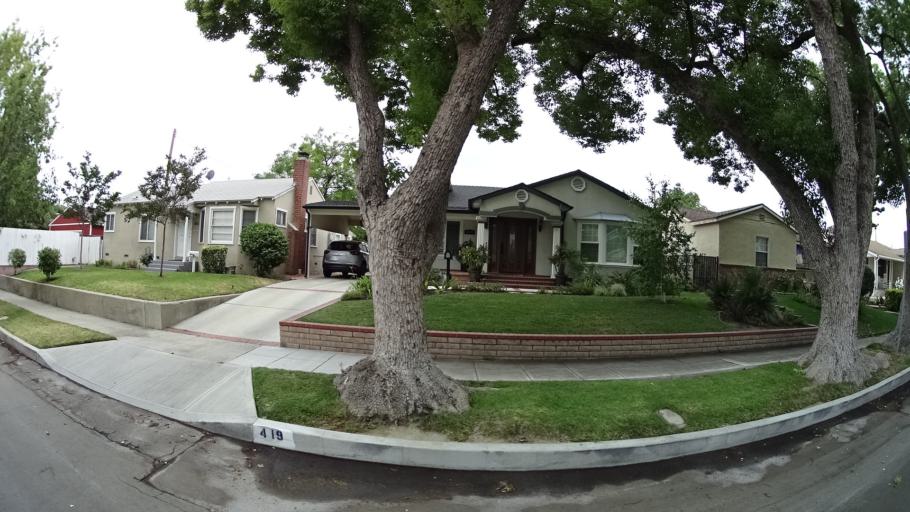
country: US
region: California
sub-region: Los Angeles County
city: Burbank
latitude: 34.1720
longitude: -118.3253
